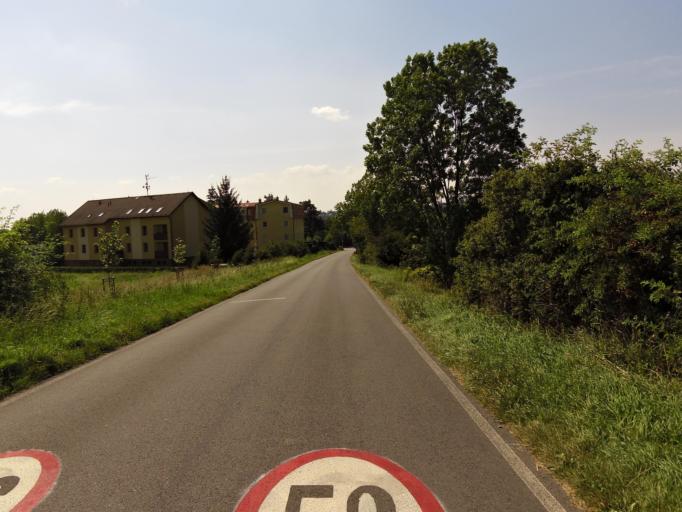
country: CZ
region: Central Bohemia
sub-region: Okres Praha-Vychod
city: Mnichovice
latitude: 49.9400
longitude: 14.7166
